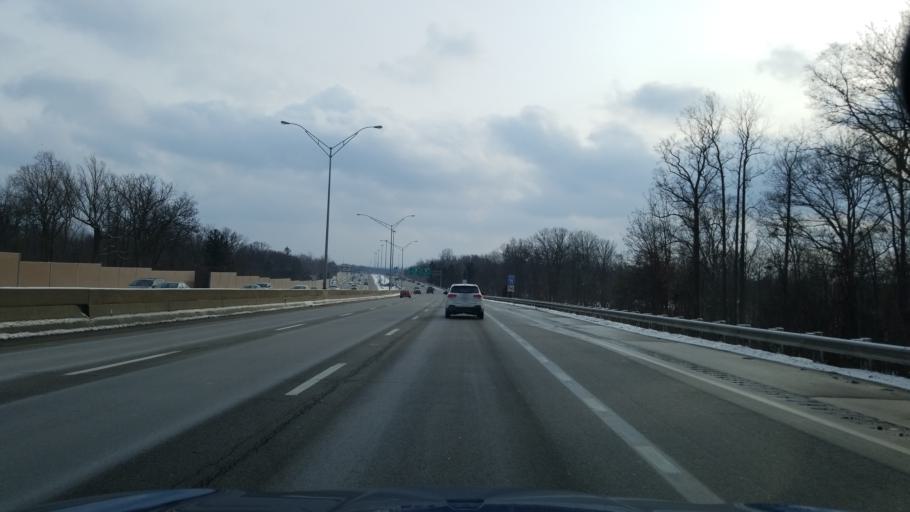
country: US
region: Ohio
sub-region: Cuyahoga County
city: Middleburg Heights
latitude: 41.3658
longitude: -81.8218
